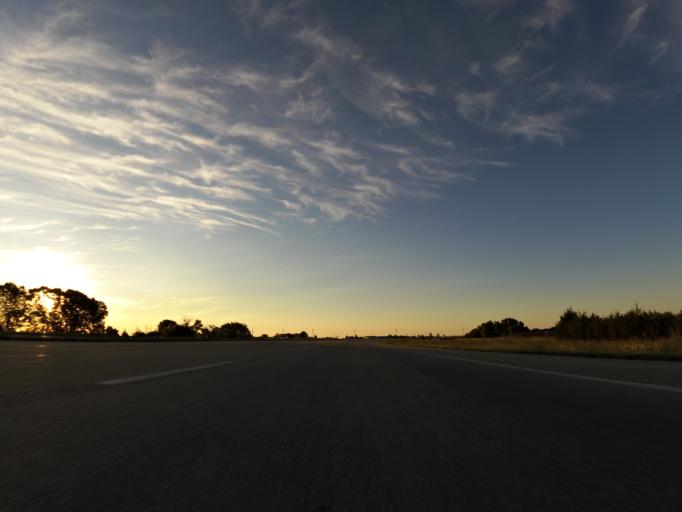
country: US
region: Kansas
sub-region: Reno County
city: South Hutchinson
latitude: 37.9492
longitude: -97.8903
